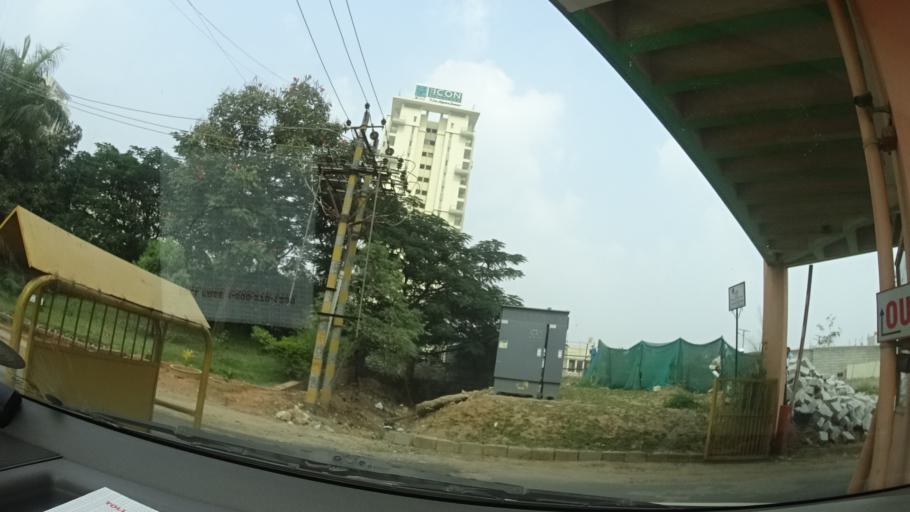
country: IN
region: Karnataka
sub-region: Bangalore Urban
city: Yelahanka
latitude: 13.0459
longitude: 77.6265
